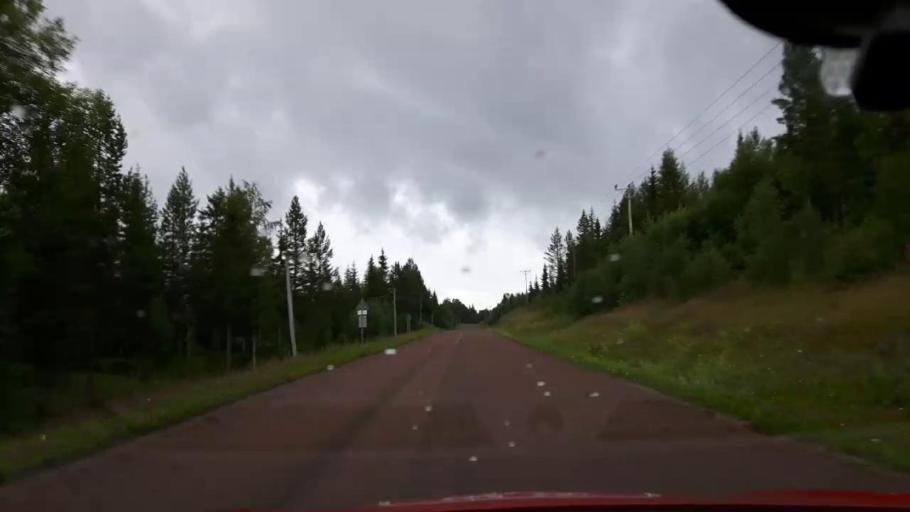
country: SE
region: Jaemtland
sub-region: Are Kommun
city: Jarpen
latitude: 63.3267
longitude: 13.6934
